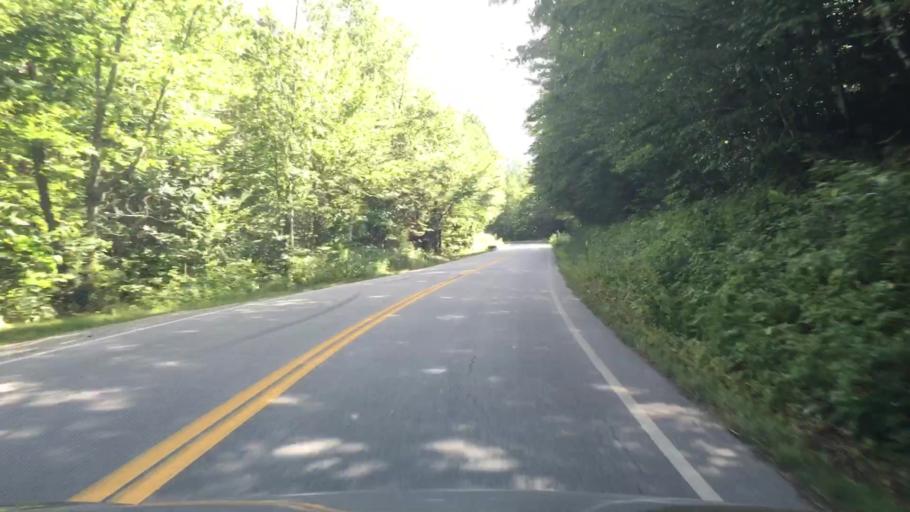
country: US
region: New Hampshire
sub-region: Carroll County
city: Tamworth
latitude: 44.0242
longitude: -71.3211
